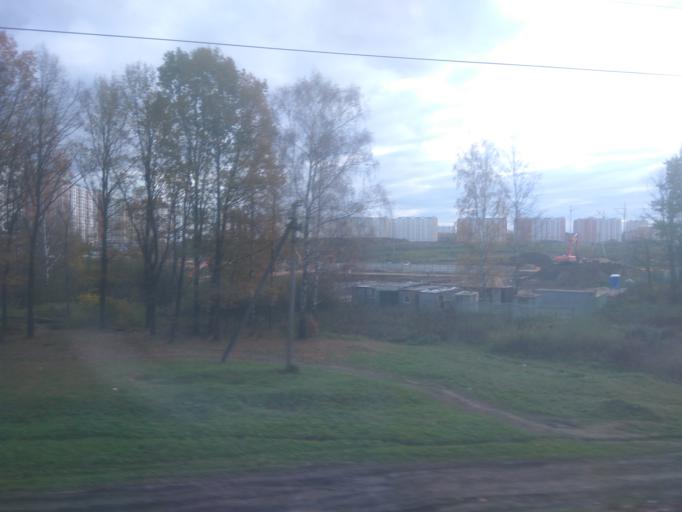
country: RU
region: Moscow
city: Novo-Peredelkino
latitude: 55.6464
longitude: 37.3249
